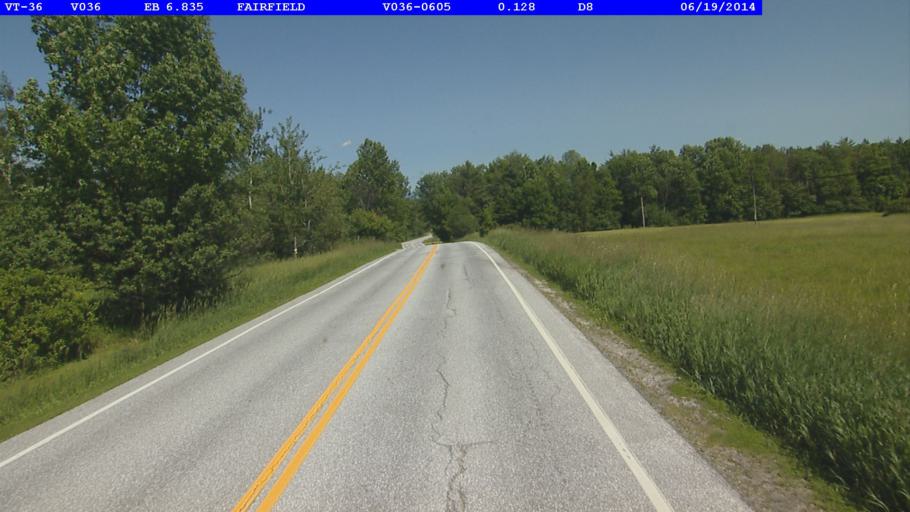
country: US
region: Vermont
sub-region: Franklin County
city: Saint Albans
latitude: 44.7900
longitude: -73.0292
